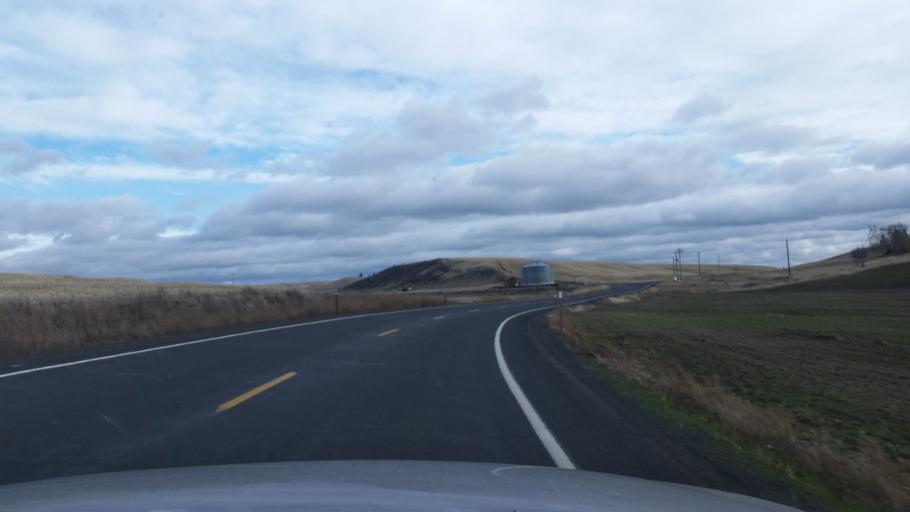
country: US
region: Washington
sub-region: Lincoln County
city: Davenport
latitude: 47.3585
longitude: -118.0421
